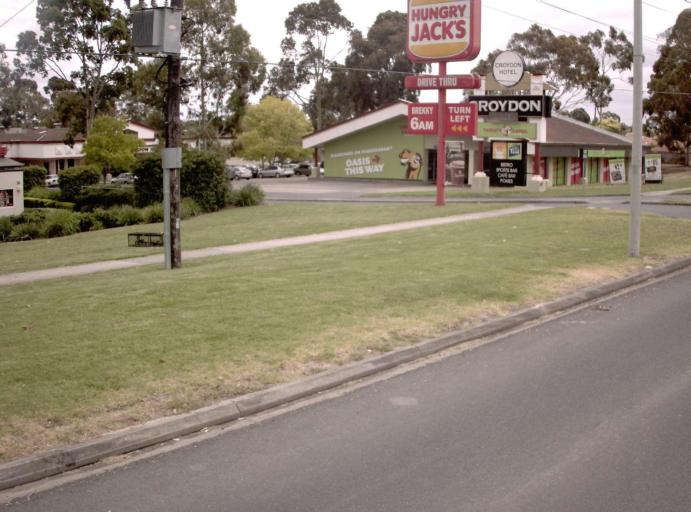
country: AU
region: Victoria
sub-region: Maroondah
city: Croydon Hills
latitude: -37.7915
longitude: 145.2628
